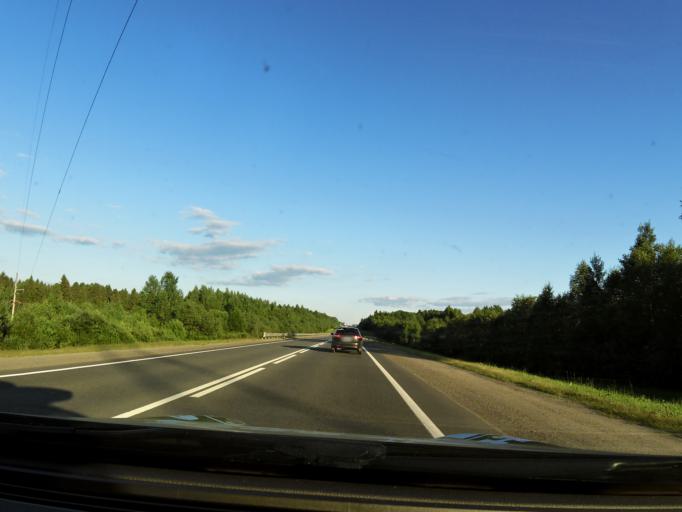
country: RU
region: Vologda
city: Vologda
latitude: 59.1306
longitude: 39.9591
